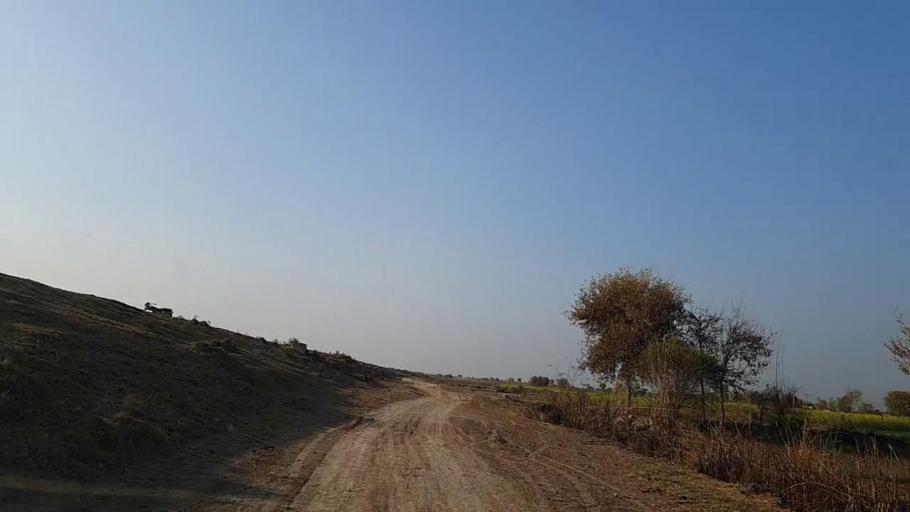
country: PK
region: Sindh
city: Sakrand
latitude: 26.1014
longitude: 68.3667
